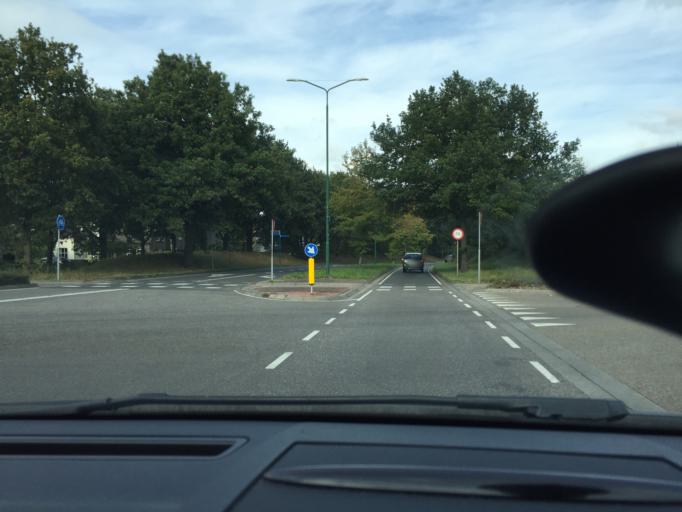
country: NL
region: North Brabant
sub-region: Gemeente Nuenen, Gerwen en Nederwetten
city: Nuenen
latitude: 51.4754
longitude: 5.5587
